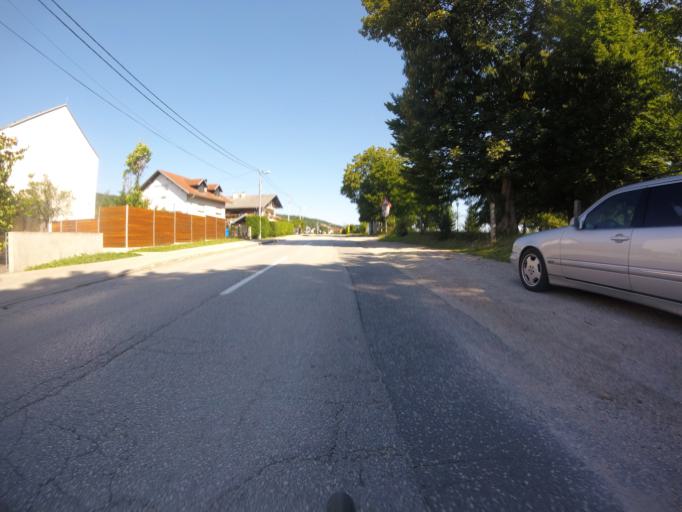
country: HR
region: Zagrebacka
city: Bregana
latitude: 45.8299
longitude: 15.6921
